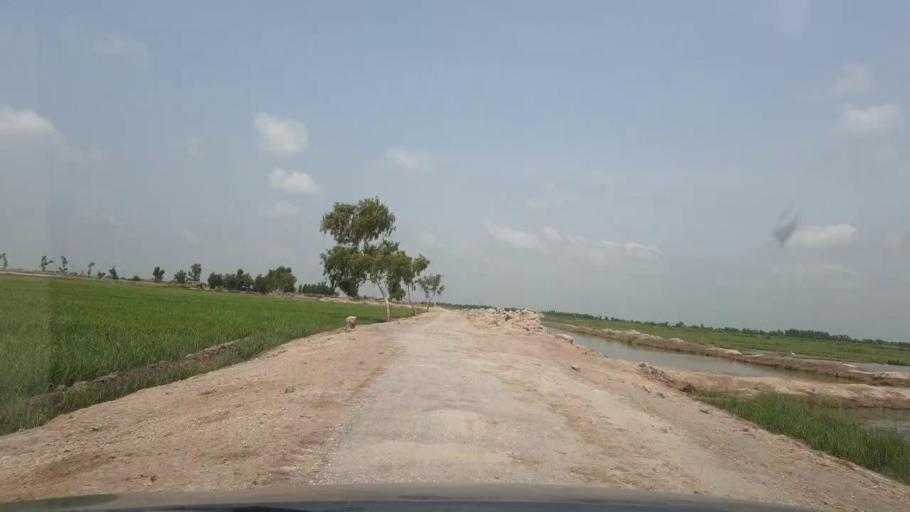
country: PK
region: Sindh
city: Ratodero
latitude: 27.9154
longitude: 68.3128
